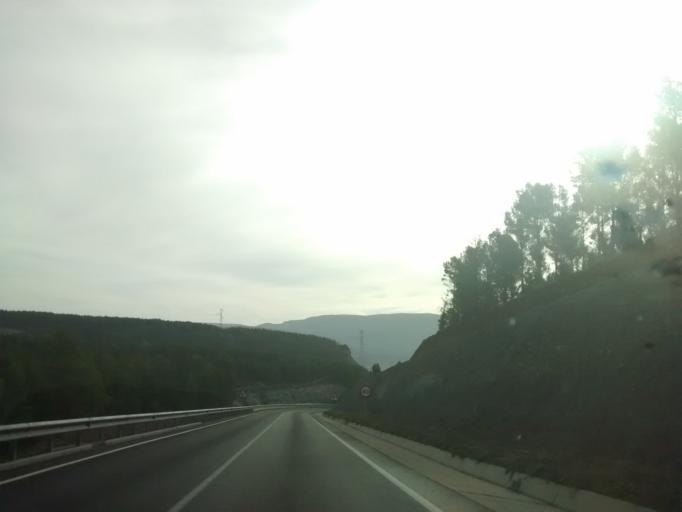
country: ES
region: Aragon
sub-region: Provincia de Zaragoza
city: Undues de Lerda
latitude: 42.6189
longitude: -1.1138
